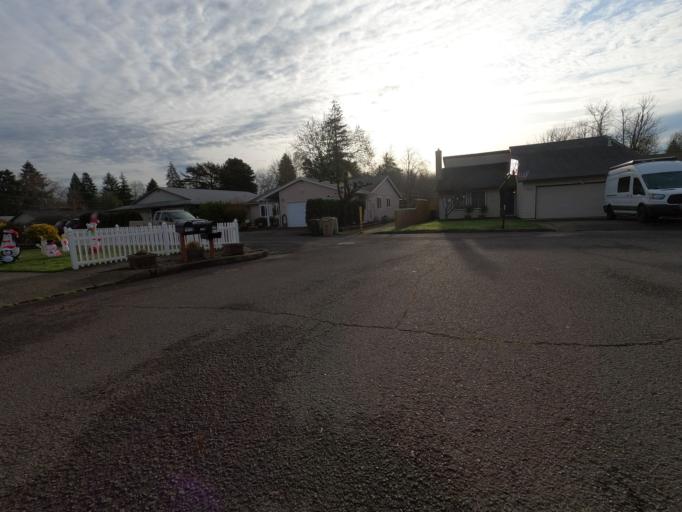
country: US
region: Oregon
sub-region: Clackamas County
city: Jennings Lodge
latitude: 45.3924
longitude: -122.6060
